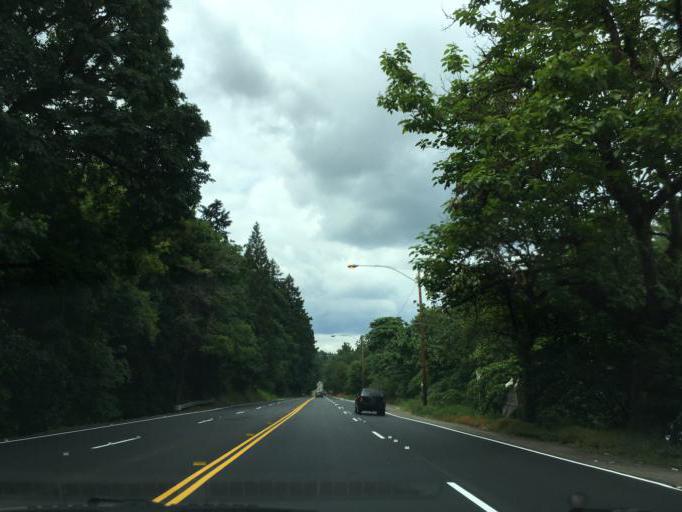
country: US
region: Oregon
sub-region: Clackamas County
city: Milwaukie
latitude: 45.4555
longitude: -122.6625
